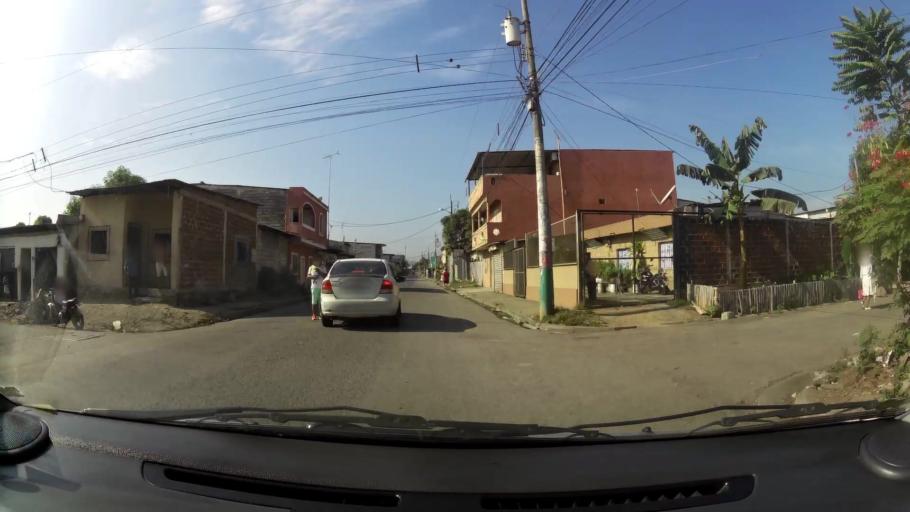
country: EC
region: Guayas
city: Eloy Alfaro
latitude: -2.0845
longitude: -79.9269
